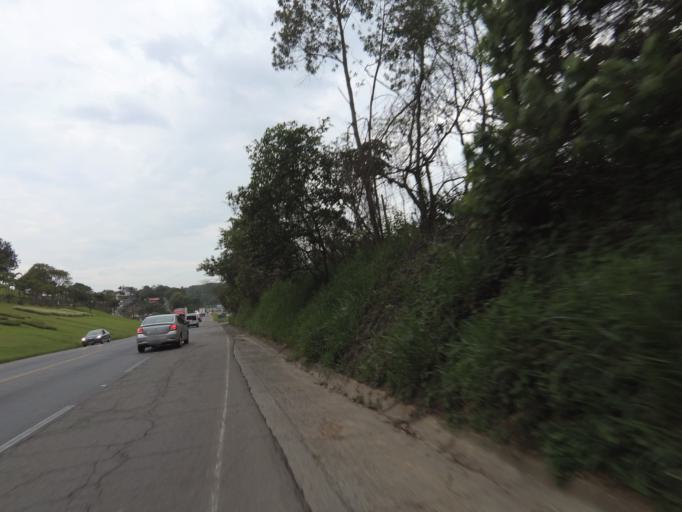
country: BR
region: Santa Catarina
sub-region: Blumenau
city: Blumenau
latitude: -26.8607
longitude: -49.0535
